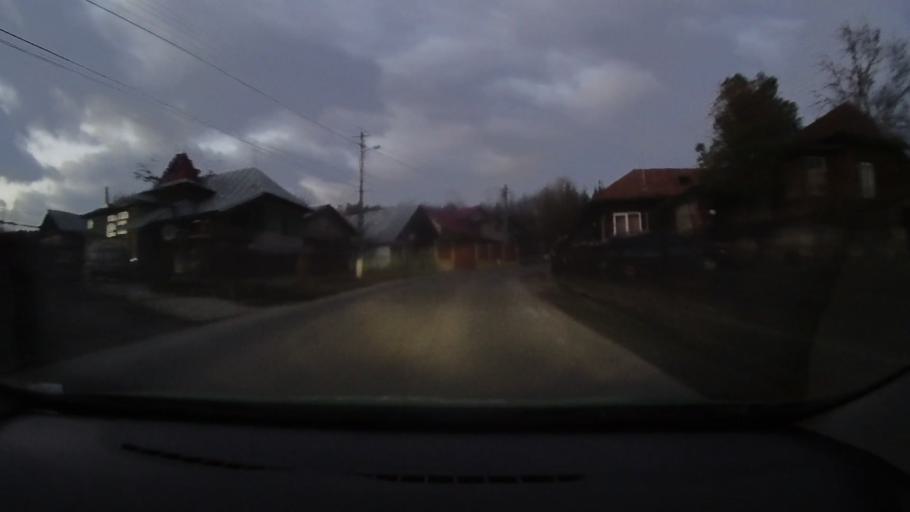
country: RO
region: Prahova
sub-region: Comuna Poiana Campina
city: Poiana Campina
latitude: 45.1241
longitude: 25.6757
